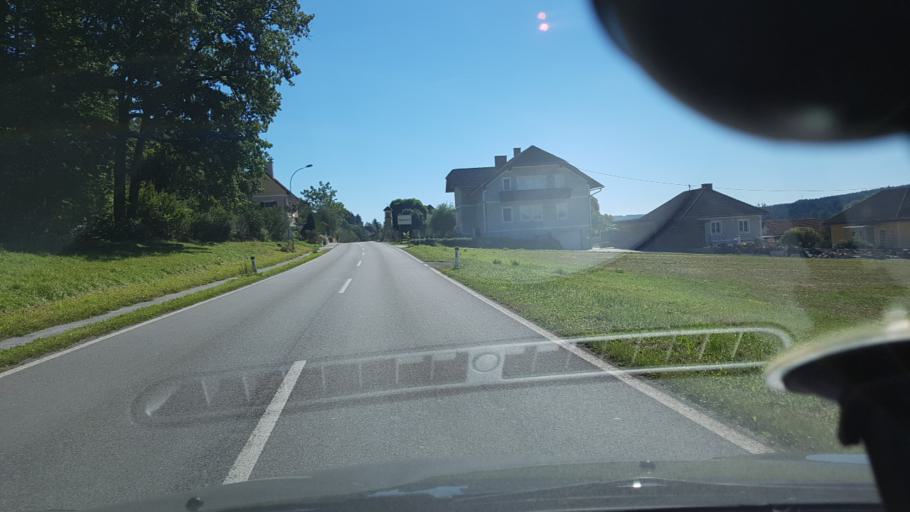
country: AT
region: Styria
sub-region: Politischer Bezirk Weiz
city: Oberrettenbach
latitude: 47.1274
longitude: 15.8090
